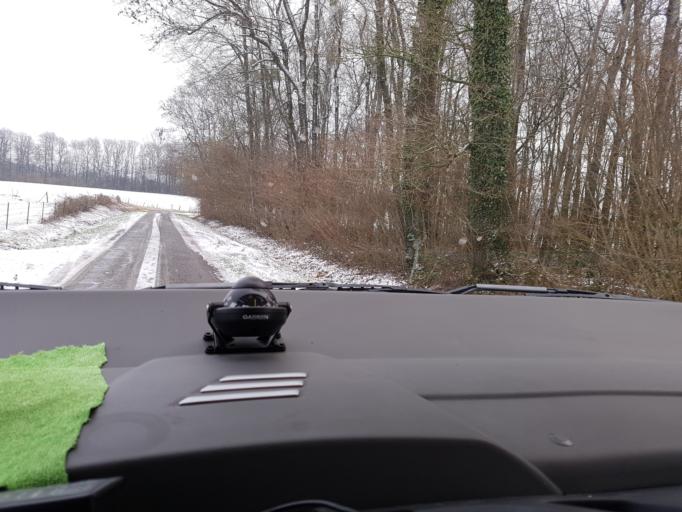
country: FR
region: Champagne-Ardenne
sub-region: Departement des Ardennes
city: Signy-le-Petit
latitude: 49.8318
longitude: 4.3925
